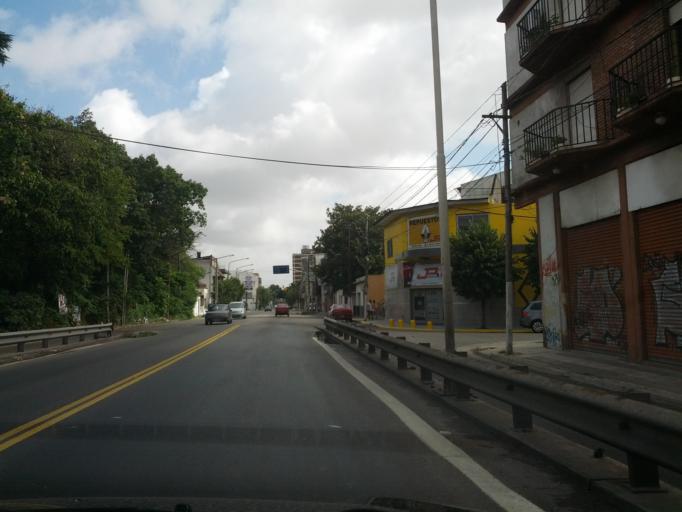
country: AR
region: Buenos Aires
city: San Justo
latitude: -34.6383
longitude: -58.5513
